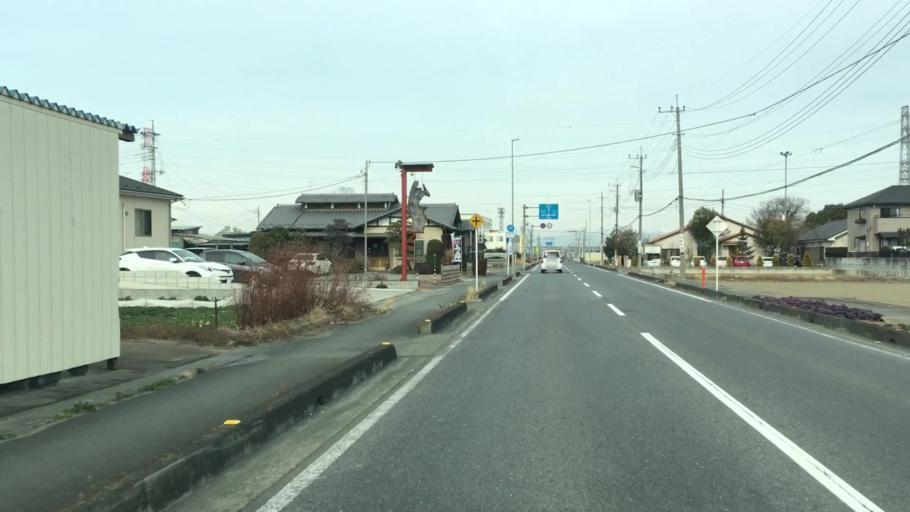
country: JP
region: Saitama
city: Fukayacho
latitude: 36.1466
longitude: 139.3227
